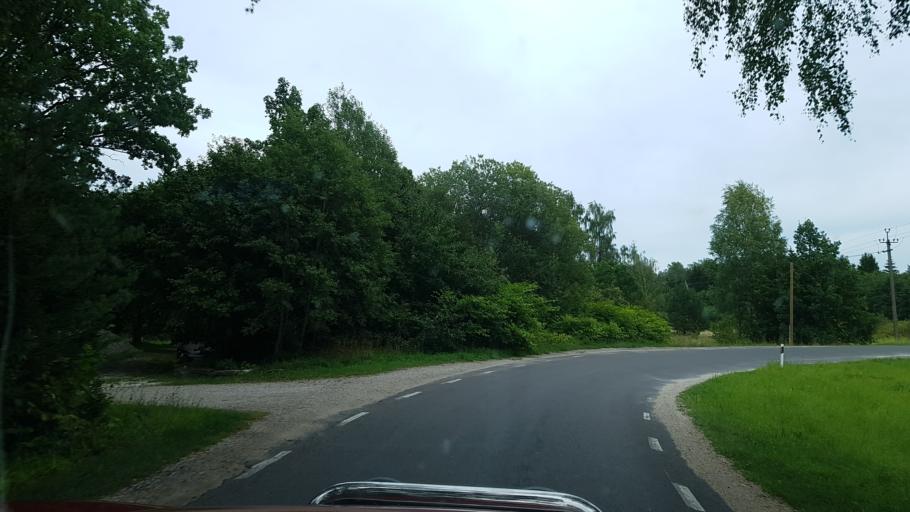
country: EE
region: Laeaene
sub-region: Ridala Parish
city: Uuemoisa
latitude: 58.9499
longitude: 23.7270
